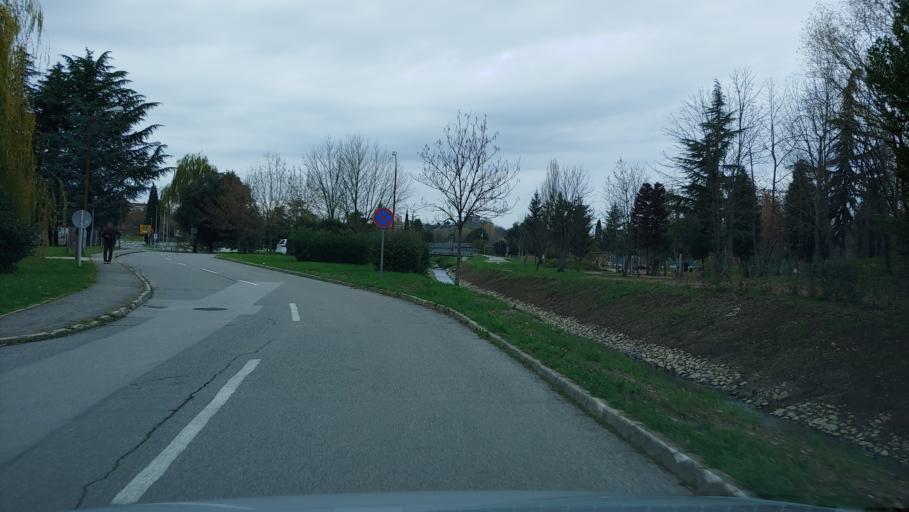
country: SI
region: Sempeter-Vrtojba
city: Sempeter pri Gorici
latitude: 45.9323
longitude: 13.6415
